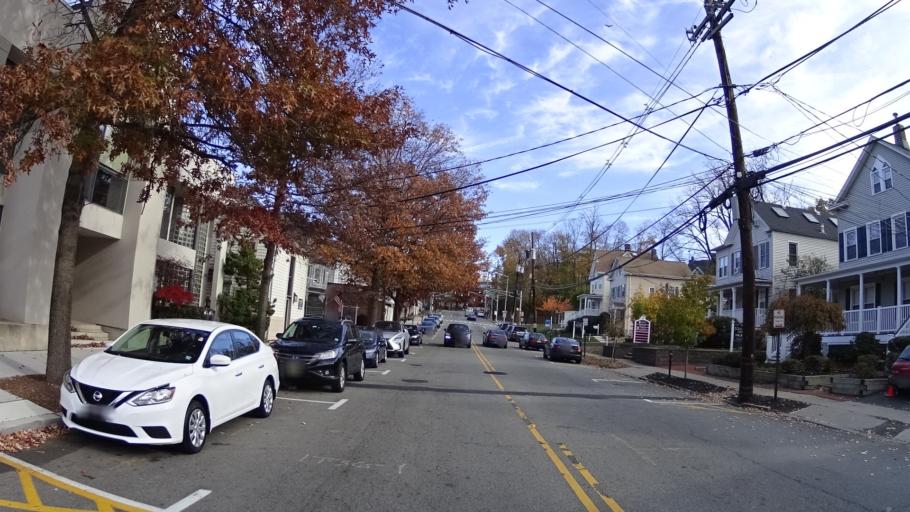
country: US
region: New Jersey
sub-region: Morris County
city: Morristown
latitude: 40.7991
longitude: -74.4864
